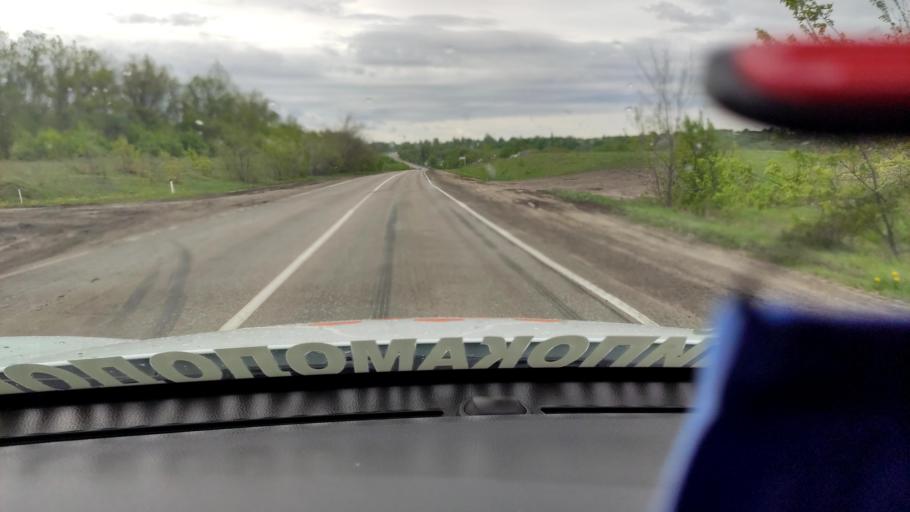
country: RU
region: Voronezj
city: Imeni Pervogo Maya
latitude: 50.7605
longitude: 39.3899
